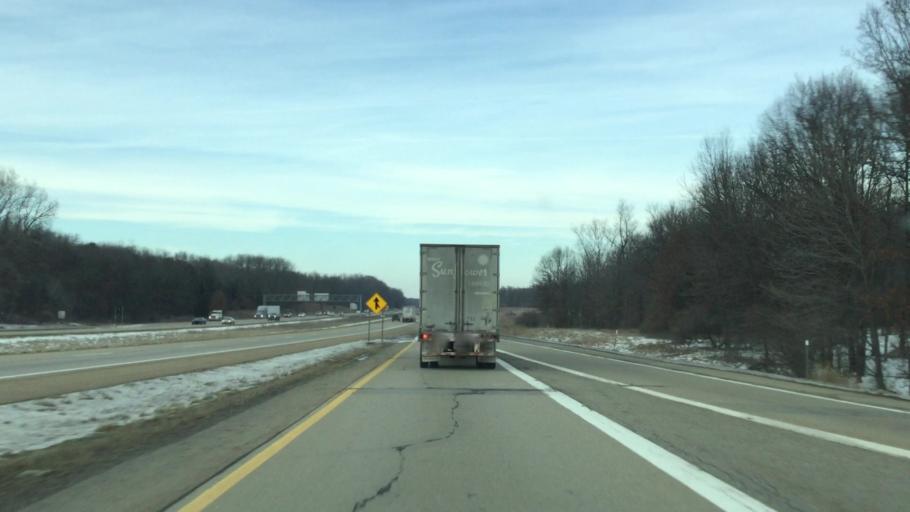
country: US
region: Michigan
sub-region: Calhoun County
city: Marshall
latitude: 42.3013
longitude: -84.9957
